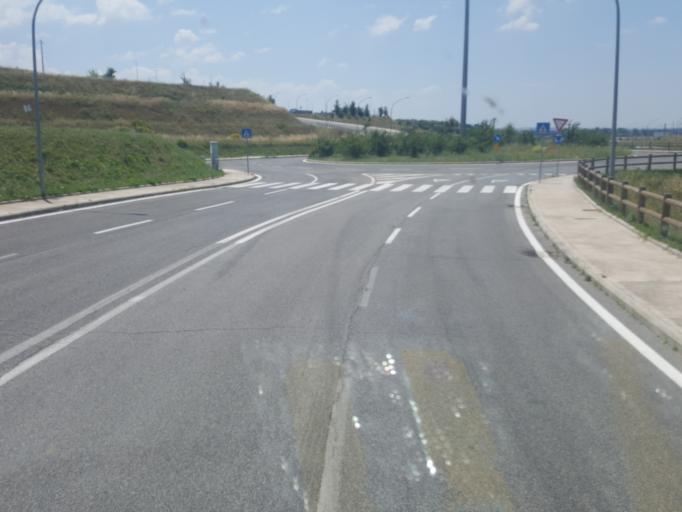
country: IT
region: Latium
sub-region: Citta metropolitana di Roma Capitale
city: Fiano Romano
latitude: 42.1665
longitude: 12.6498
